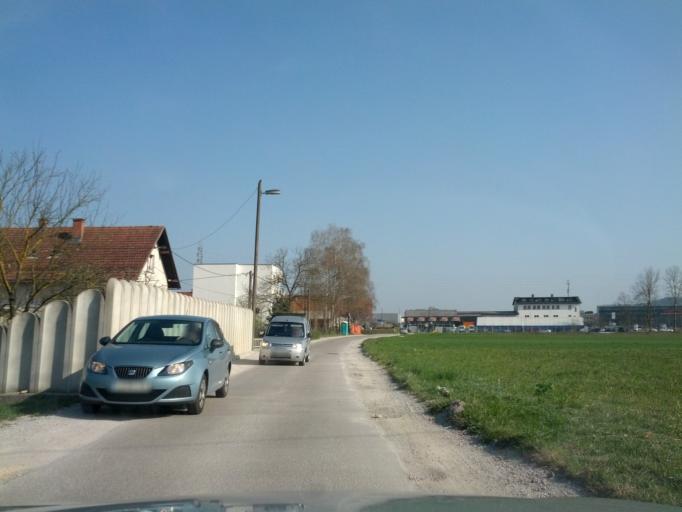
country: SI
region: Ljubljana
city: Ljubljana
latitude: 46.0920
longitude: 14.4766
